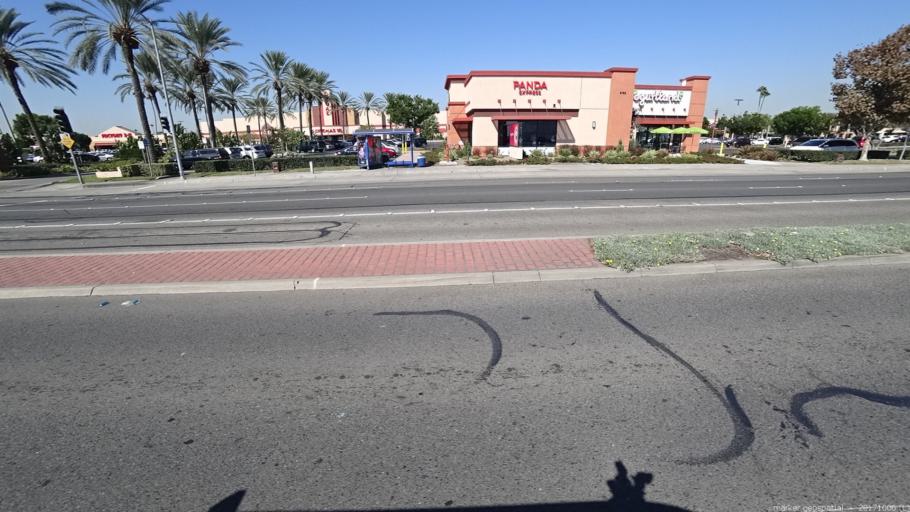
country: US
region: California
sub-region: Orange County
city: Garden Grove
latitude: 33.7885
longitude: -117.9626
